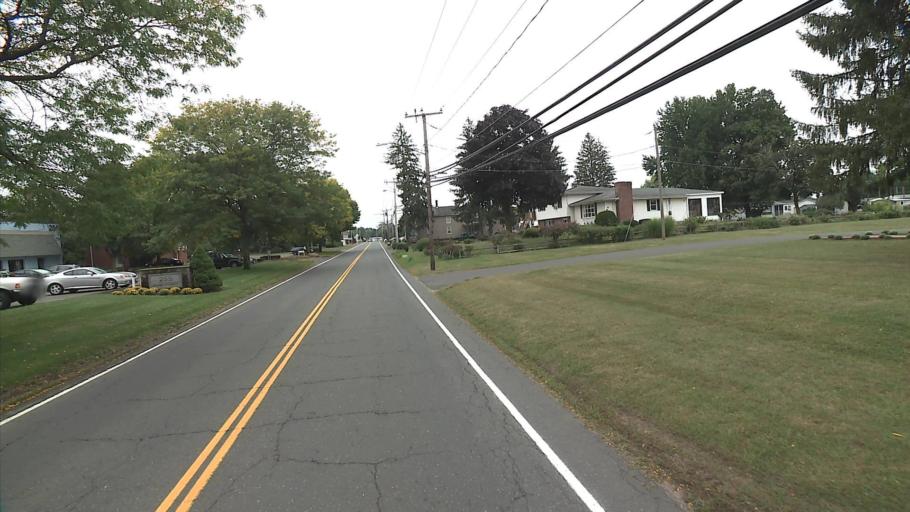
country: US
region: Connecticut
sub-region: Hartford County
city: Windsor Locks
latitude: 41.9169
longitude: -72.6148
